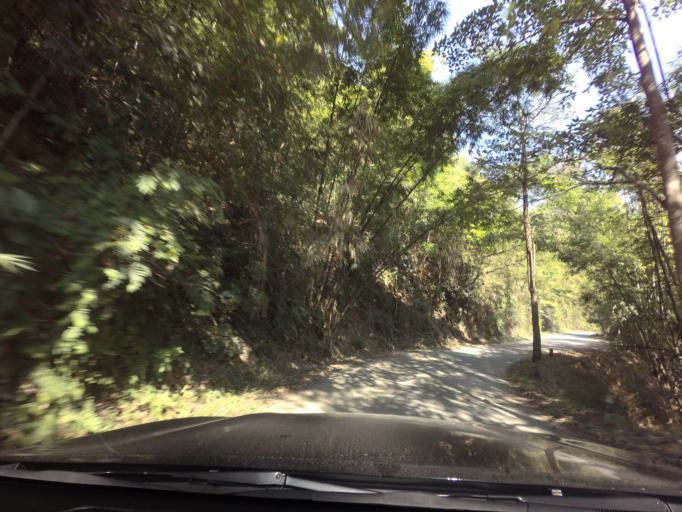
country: TH
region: Kanchanaburi
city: Thong Pha Phum
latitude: 14.6983
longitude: 98.4581
